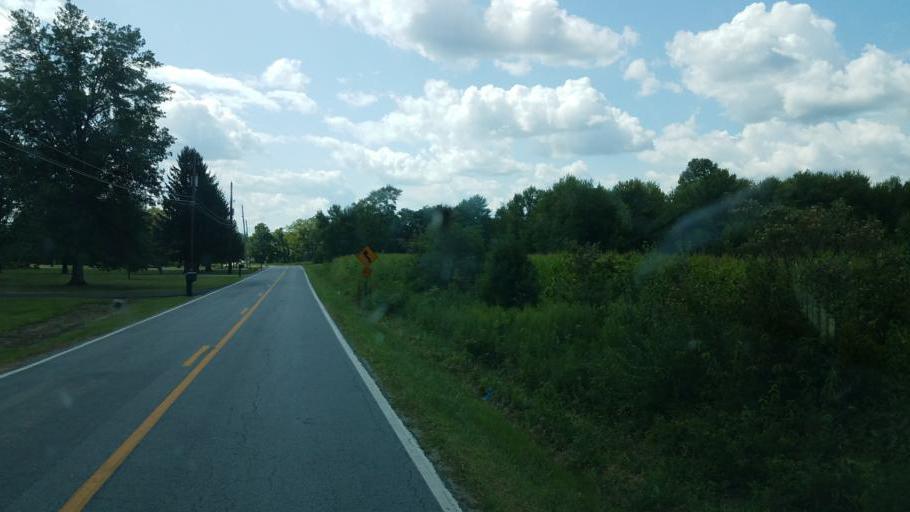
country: US
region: Ohio
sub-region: Delaware County
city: Lewis Center
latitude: 40.2258
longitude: -82.9857
